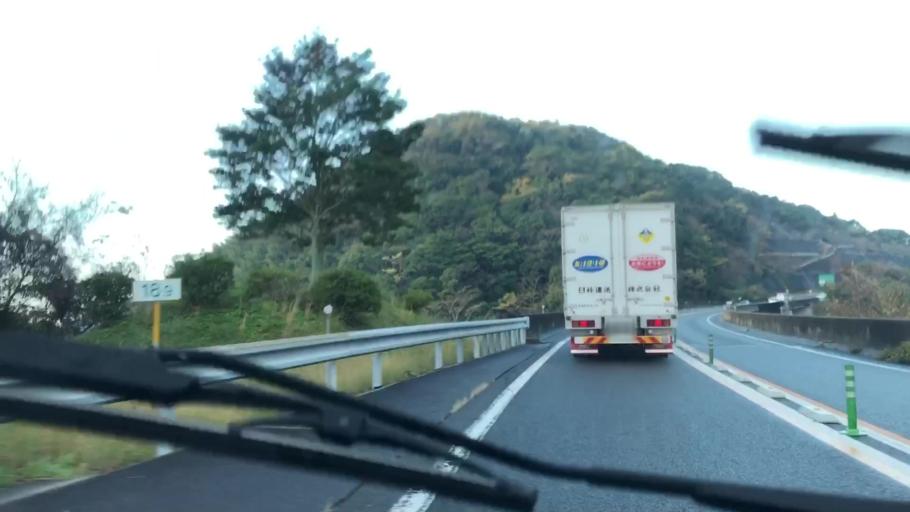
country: JP
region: Nagasaki
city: Sasebo
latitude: 33.1505
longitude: 129.8074
